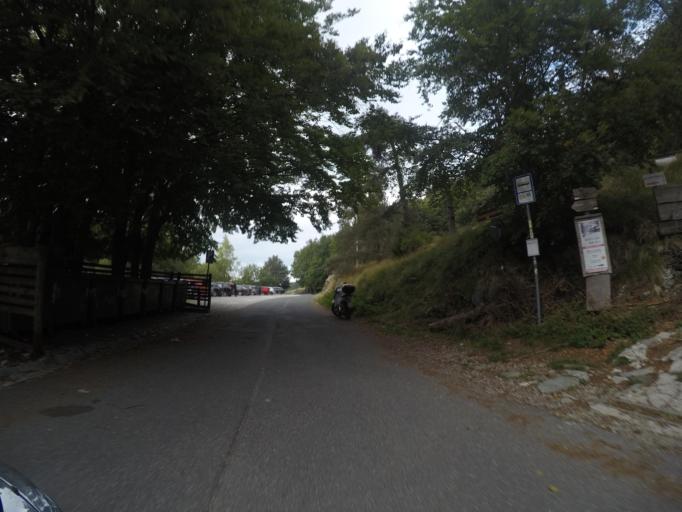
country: IT
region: Tuscany
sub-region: Provincia di Massa-Carrara
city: Carrara
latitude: 44.1198
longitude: 10.1218
